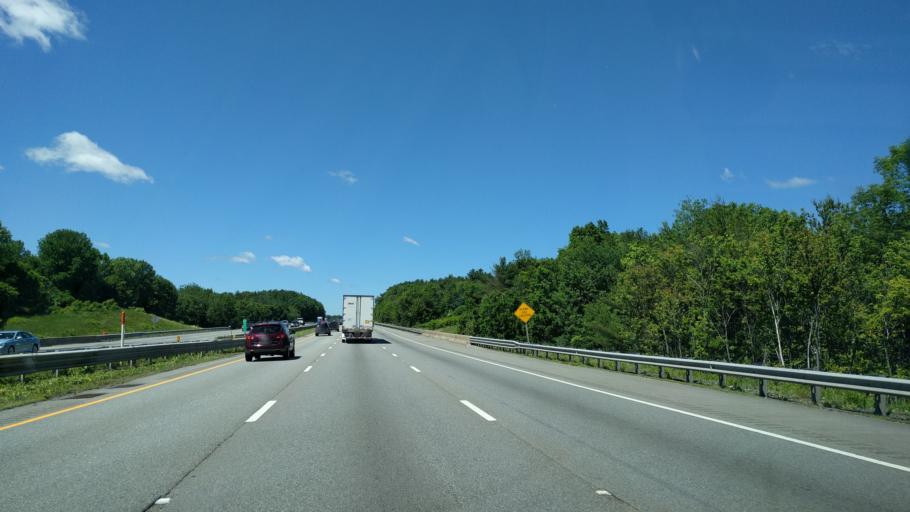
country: US
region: Massachusetts
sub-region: Worcester County
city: Charlton
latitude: 42.1516
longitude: -71.9913
